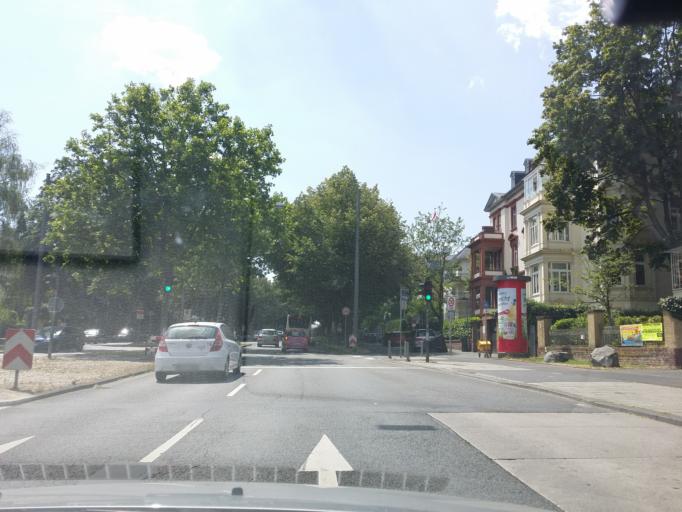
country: DE
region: Hesse
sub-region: Regierungsbezirk Darmstadt
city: Wiesbaden
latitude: 50.0696
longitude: 8.2401
